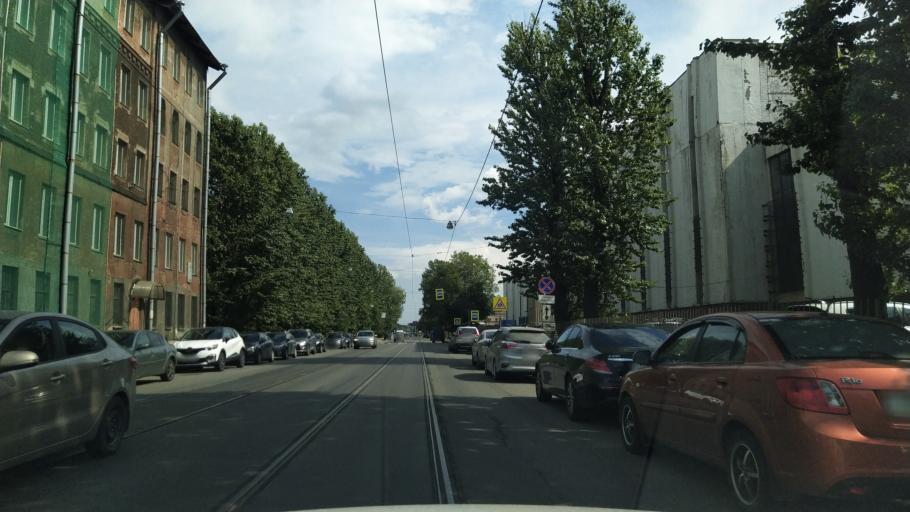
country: RU
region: Leningrad
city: Finlyandskiy
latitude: 59.9657
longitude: 30.3907
